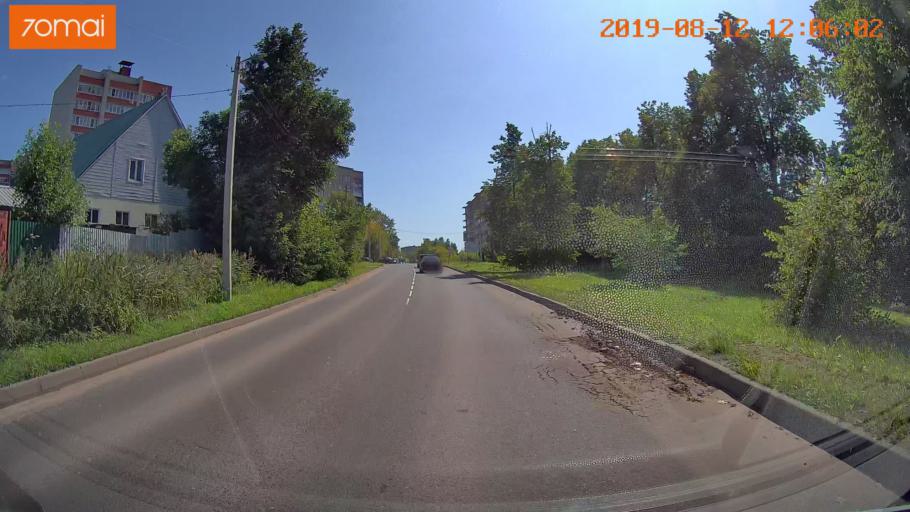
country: RU
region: Ivanovo
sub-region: Gorod Ivanovo
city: Ivanovo
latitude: 56.9901
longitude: 41.0198
